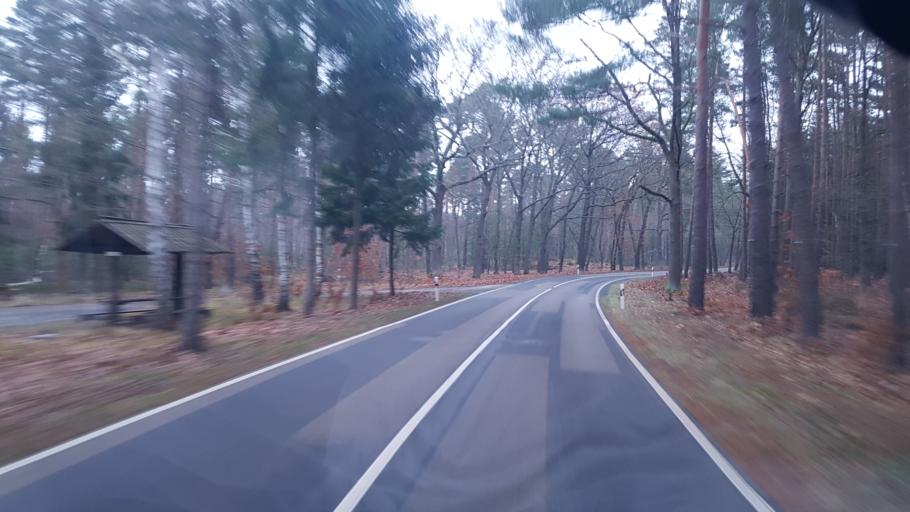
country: DE
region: Brandenburg
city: Drachhausen
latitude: 51.8705
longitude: 14.2728
